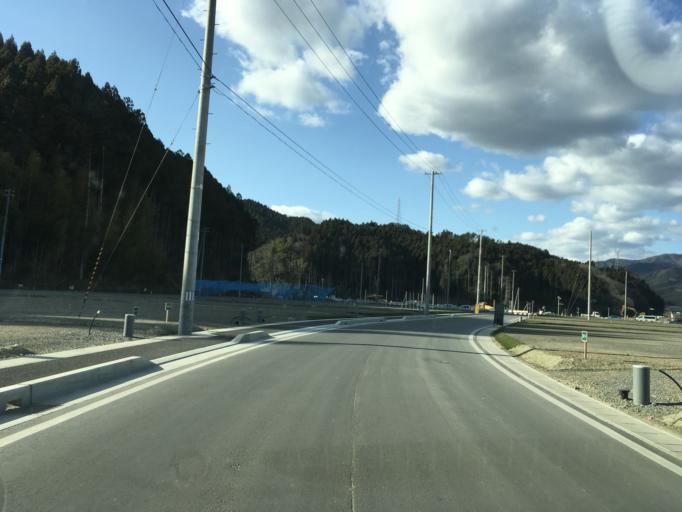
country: JP
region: Iwate
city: Ofunato
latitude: 39.0136
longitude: 141.6151
